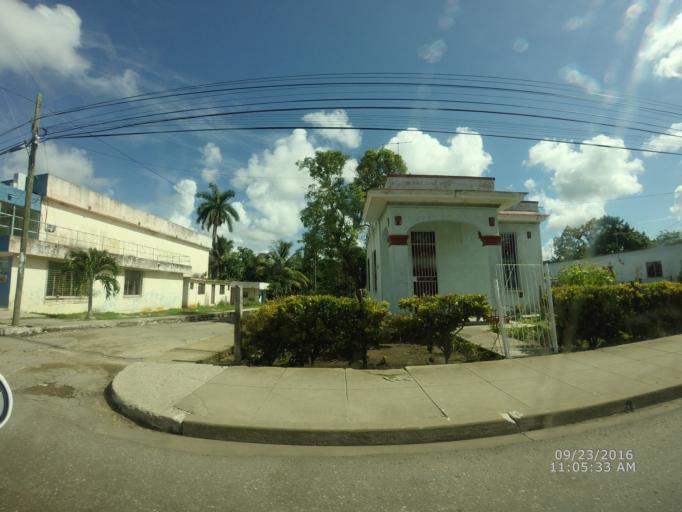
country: CU
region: Mayabeque
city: Jamaica
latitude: 23.0070
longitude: -82.2168
